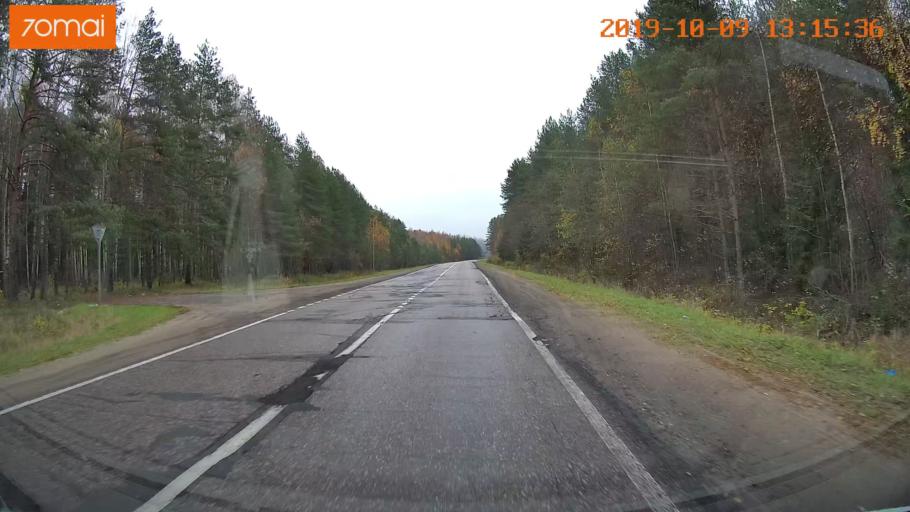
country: RU
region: Jaroslavl
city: Lyubim
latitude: 58.3667
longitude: 40.7544
